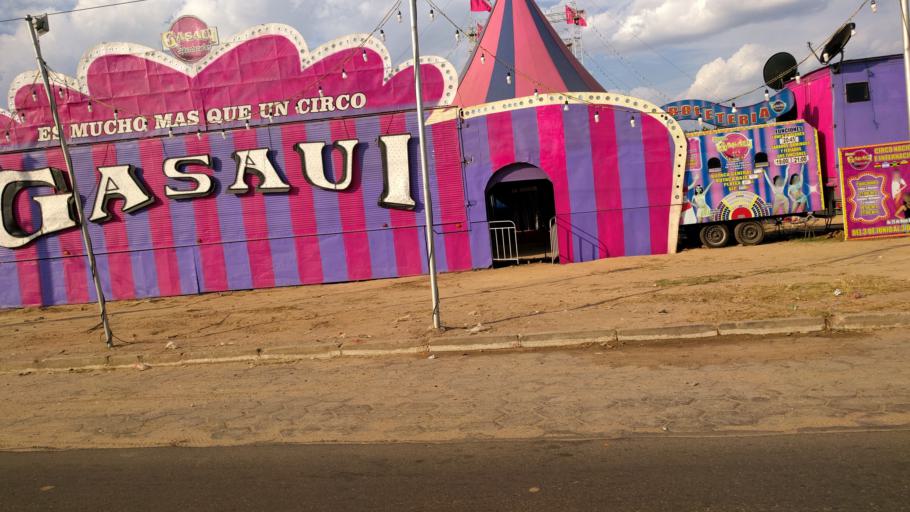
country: BO
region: Santa Cruz
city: Warnes
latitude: -17.5070
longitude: -63.1693
